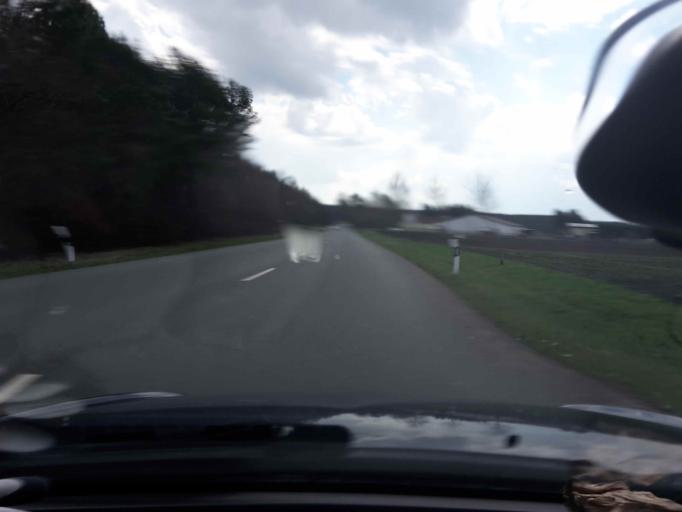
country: DE
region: Lower Saxony
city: Munster
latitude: 53.0369
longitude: 10.0590
